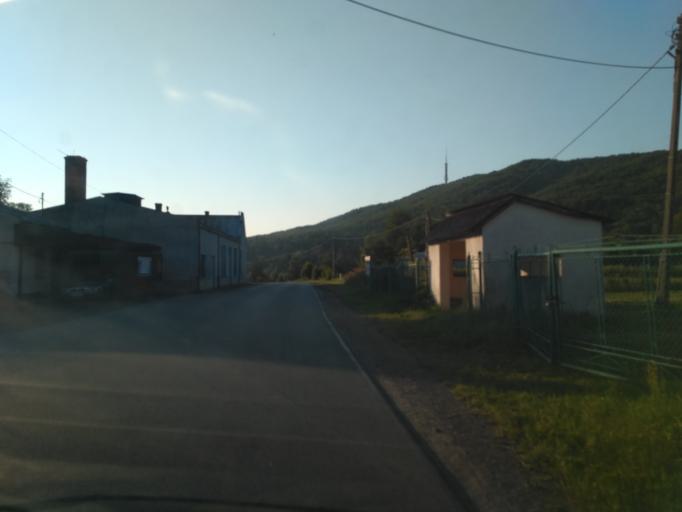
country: PL
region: Subcarpathian Voivodeship
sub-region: Powiat krosnienski
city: Korczyna
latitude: 49.7662
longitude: 21.7934
